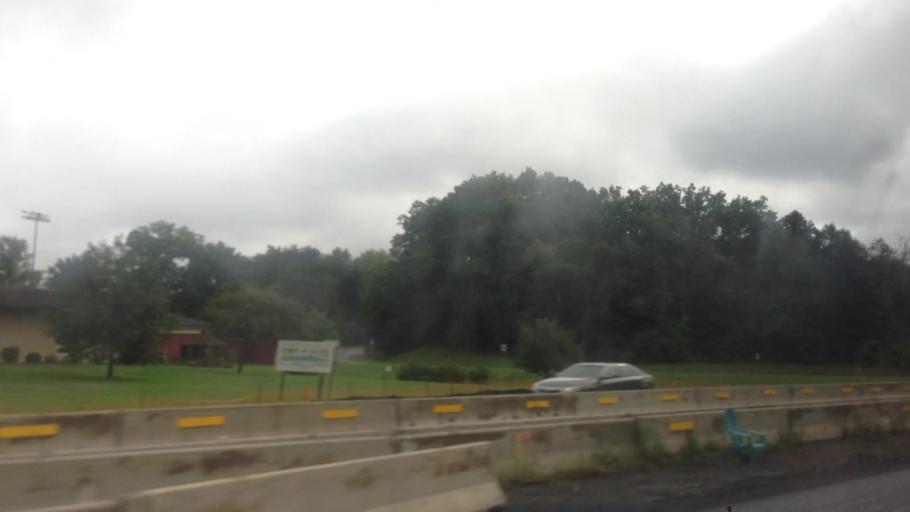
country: US
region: New York
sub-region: Ulster County
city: Lake Katrine
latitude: 41.9761
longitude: -74.0028
